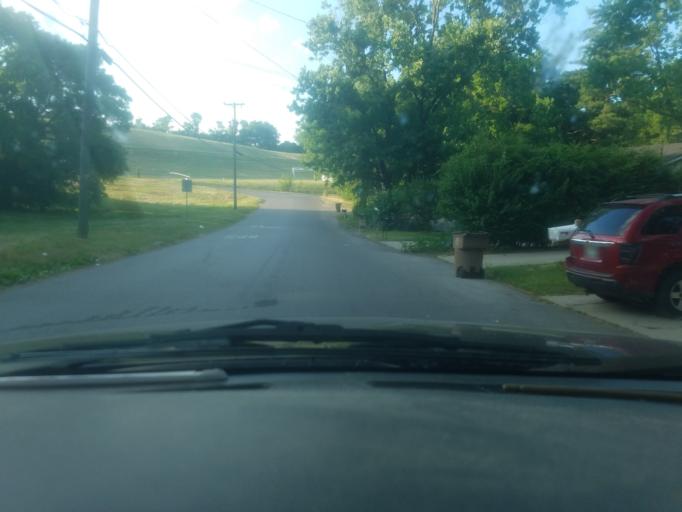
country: US
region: Tennessee
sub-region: Davidson County
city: Nashville
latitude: 36.1632
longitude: -86.8400
